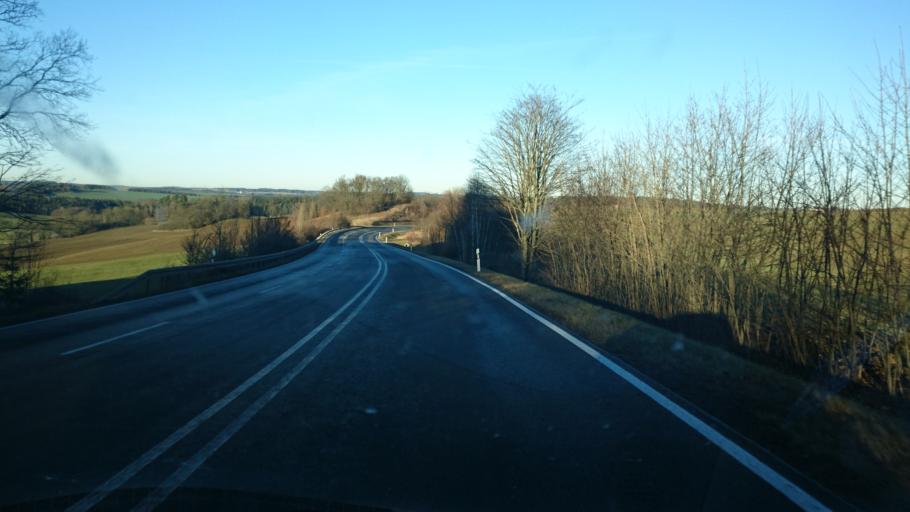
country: DE
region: Thuringia
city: Kirschkau
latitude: 50.6075
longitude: 11.9099
